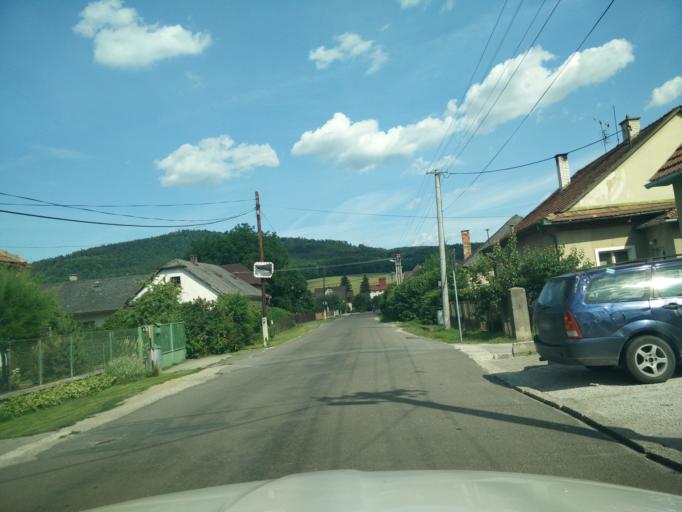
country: SK
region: Nitriansky
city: Prievidza
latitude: 48.8542
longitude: 18.6468
